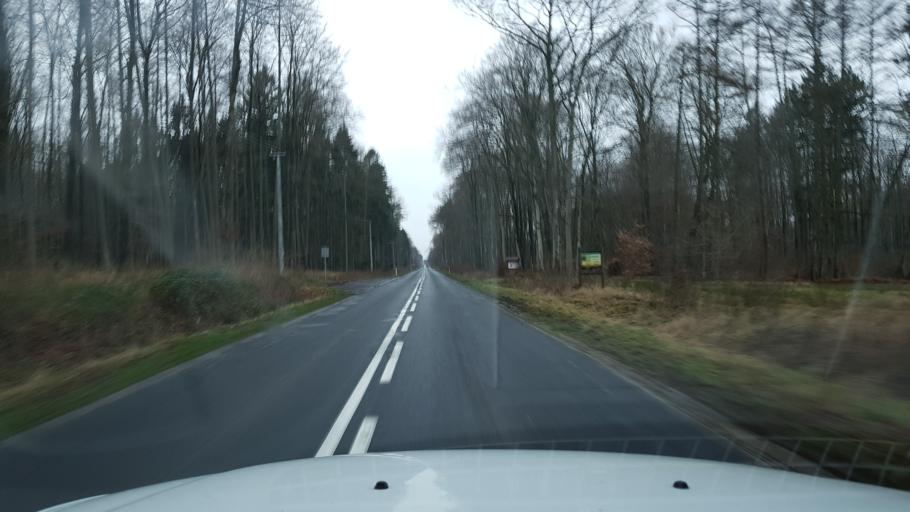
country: PL
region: West Pomeranian Voivodeship
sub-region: Powiat gryficki
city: Trzebiatow
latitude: 54.0553
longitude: 15.3595
